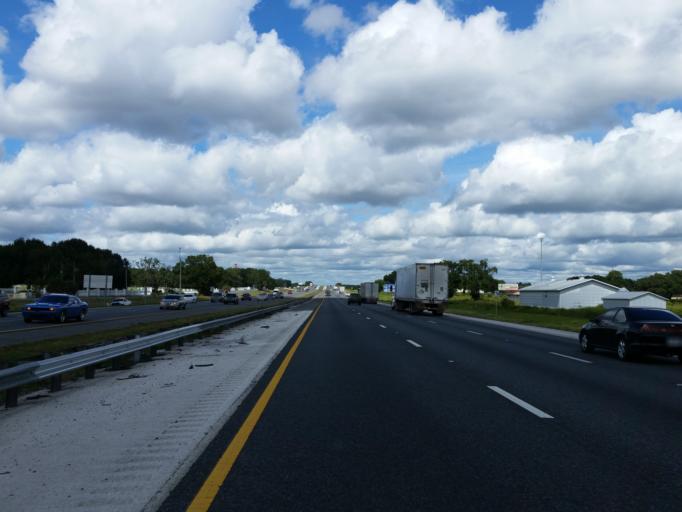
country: US
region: Florida
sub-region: Marion County
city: Belleview
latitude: 29.0157
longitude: -82.1545
